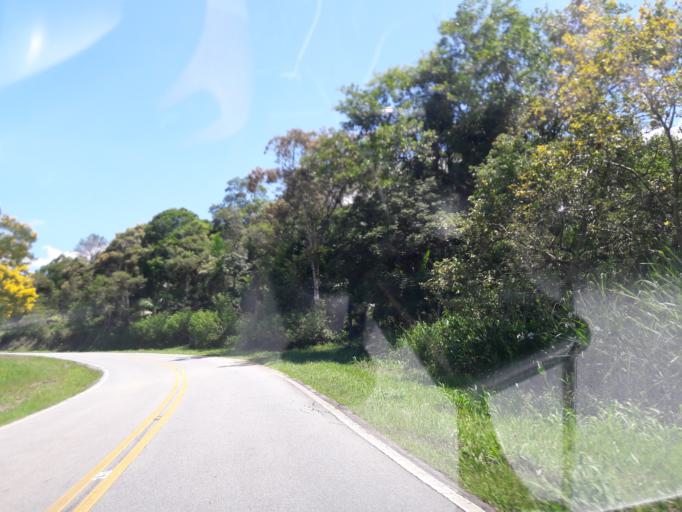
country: BR
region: Parana
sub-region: Antonina
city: Antonina
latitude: -25.5246
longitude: -48.7856
